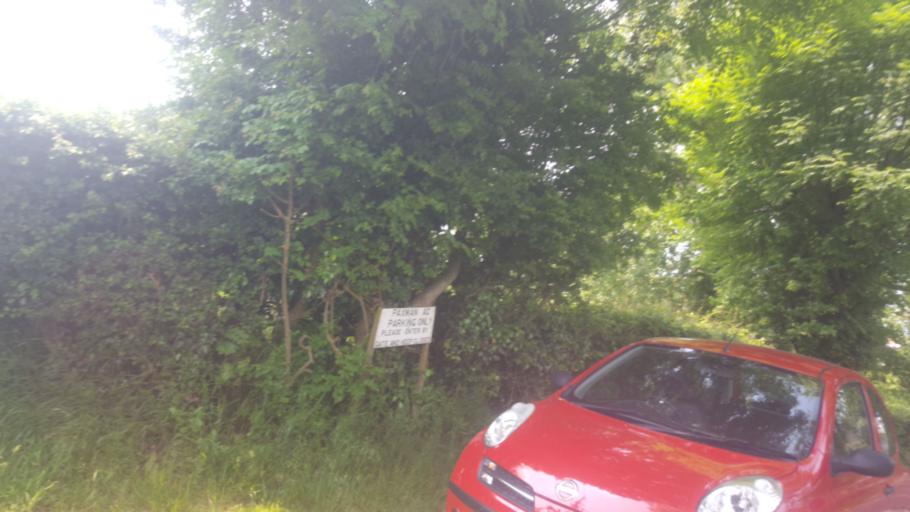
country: GB
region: England
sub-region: Essex
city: Saint Osyth
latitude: 51.7996
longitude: 1.0991
